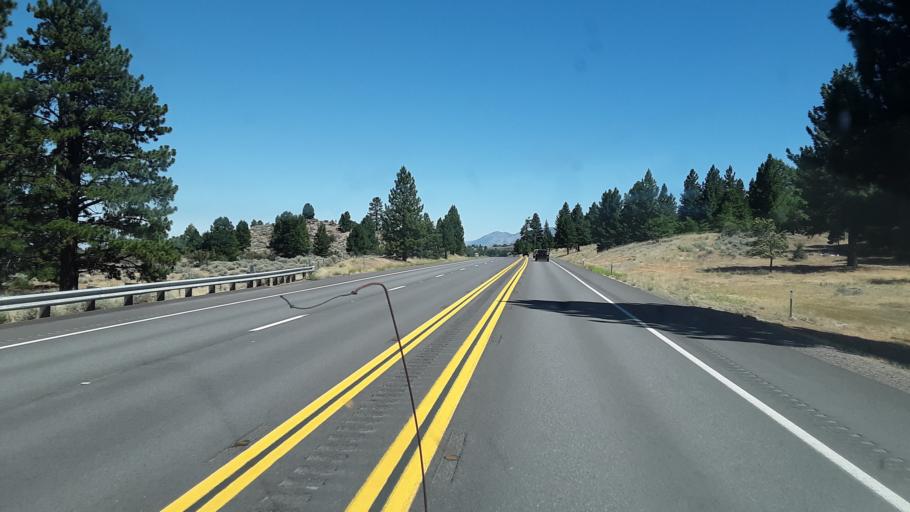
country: US
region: California
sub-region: Lassen County
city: Janesville
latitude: 40.3072
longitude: -120.5303
